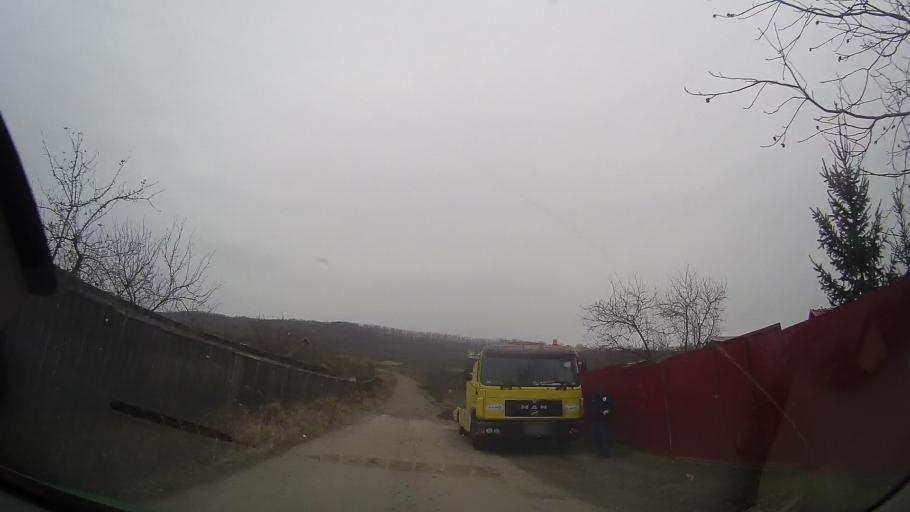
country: RO
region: Mures
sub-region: Comuna Ceausu de Campie
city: Ceausu de Campie
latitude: 46.6461
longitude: 24.4971
